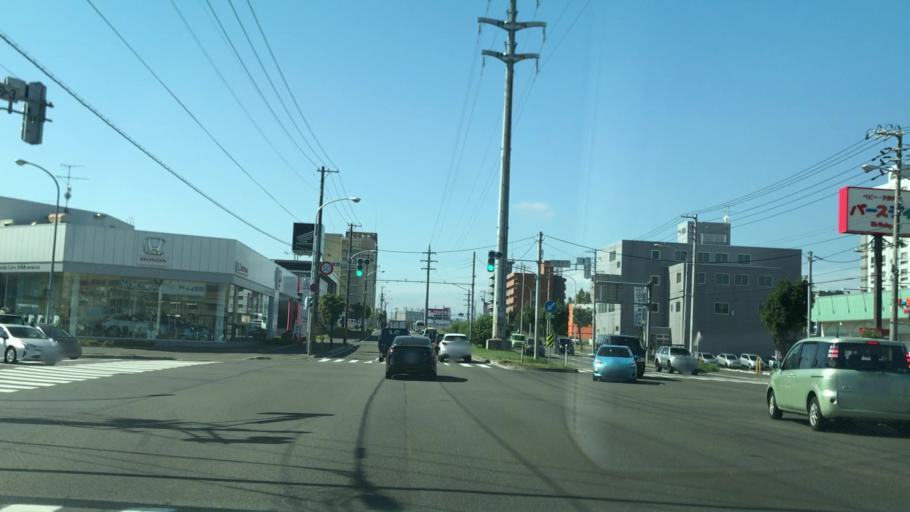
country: JP
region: Hokkaido
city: Sapporo
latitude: 43.0677
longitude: 141.4087
